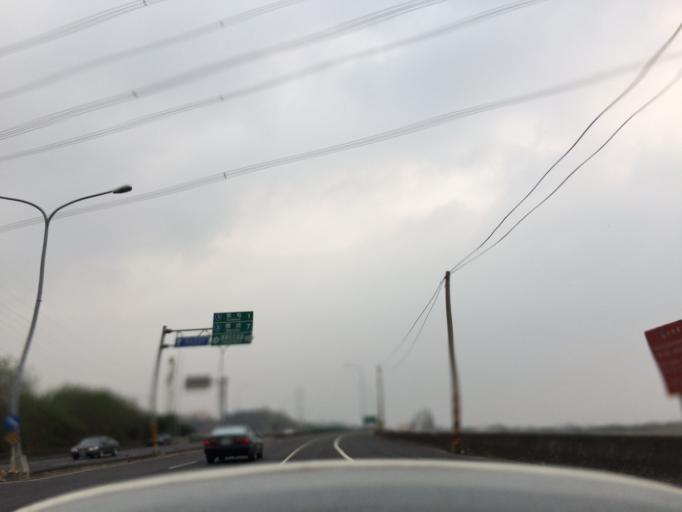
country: TW
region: Taiwan
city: Zhongxing New Village
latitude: 24.0114
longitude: 120.6957
